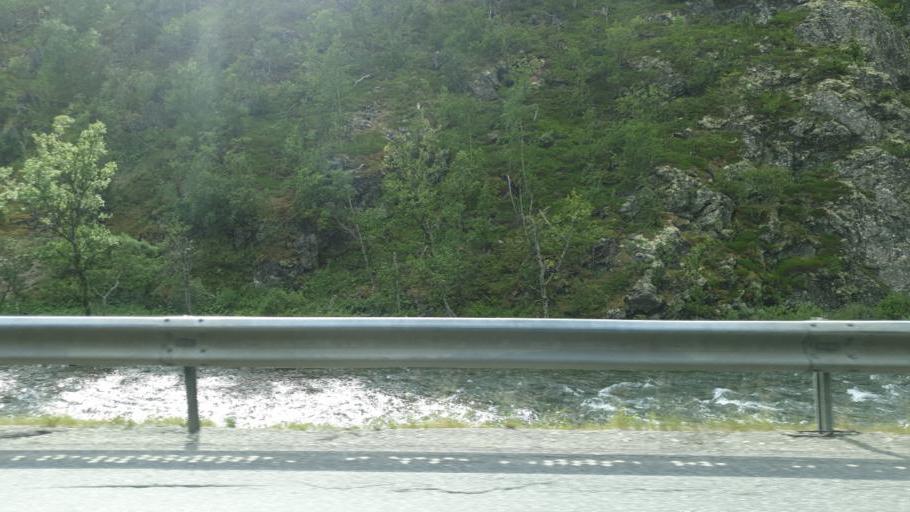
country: NO
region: Sor-Trondelag
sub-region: Oppdal
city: Oppdal
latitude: 62.3623
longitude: 9.6375
